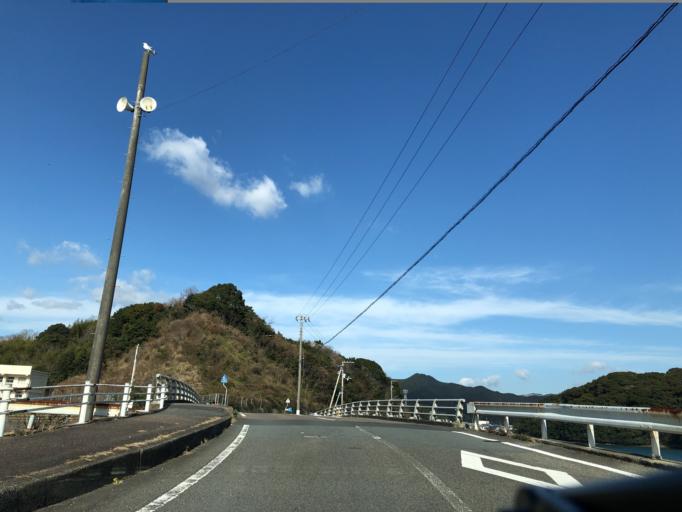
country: JP
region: Kochi
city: Sukumo
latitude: 32.9181
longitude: 132.7027
